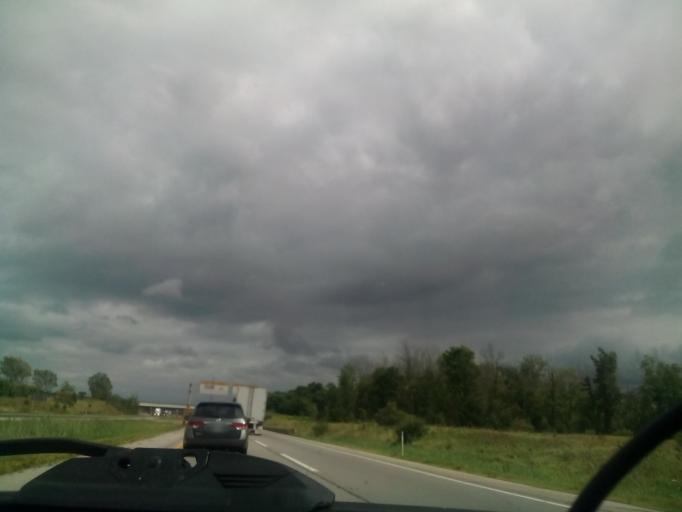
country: US
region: Indiana
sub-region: Steuben County
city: Fremont
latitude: 41.6707
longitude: -84.8631
